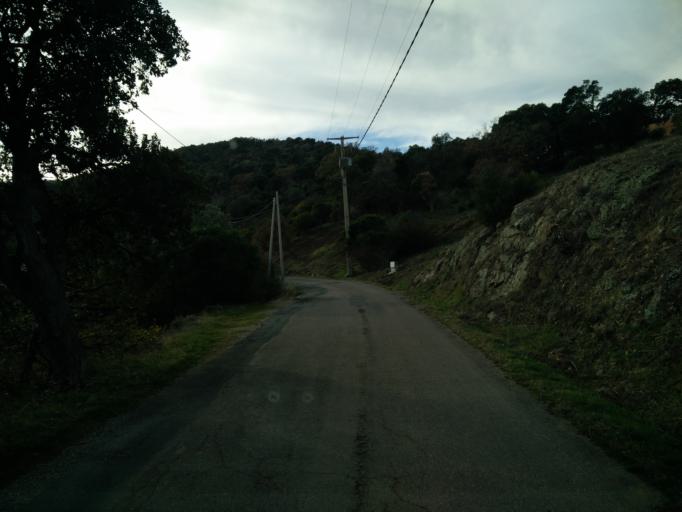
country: FR
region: Provence-Alpes-Cote d'Azur
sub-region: Departement du Var
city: Roquebrune-sur-Argens
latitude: 43.4312
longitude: 6.6398
